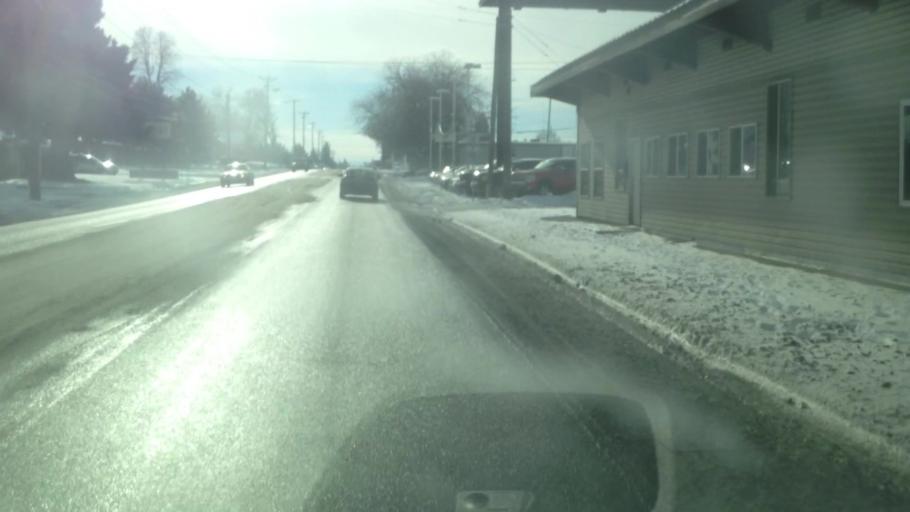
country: US
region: Idaho
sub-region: Bonneville County
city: Idaho Falls
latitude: 43.5031
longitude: -112.0239
